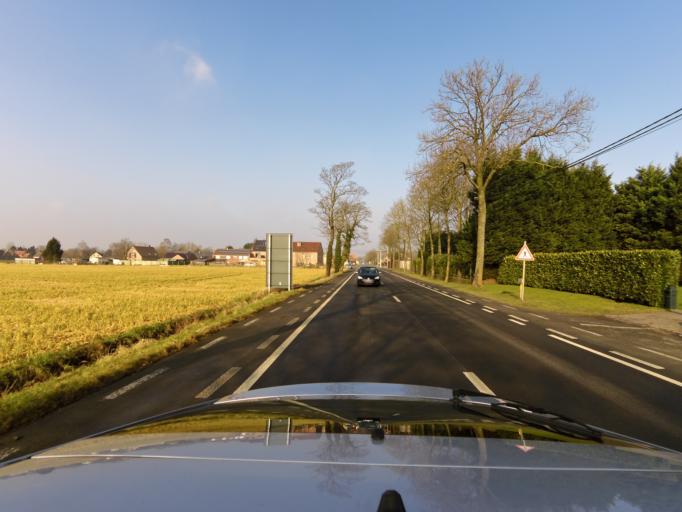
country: BE
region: Wallonia
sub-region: Province du Hainaut
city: Peruwelz
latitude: 50.5702
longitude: 3.5676
